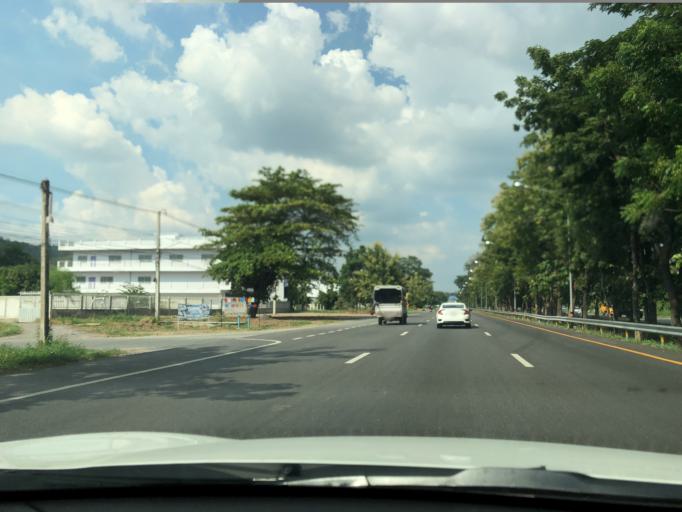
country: TH
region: Nakhon Sawan
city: Nakhon Sawan
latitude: 15.6341
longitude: 100.1296
